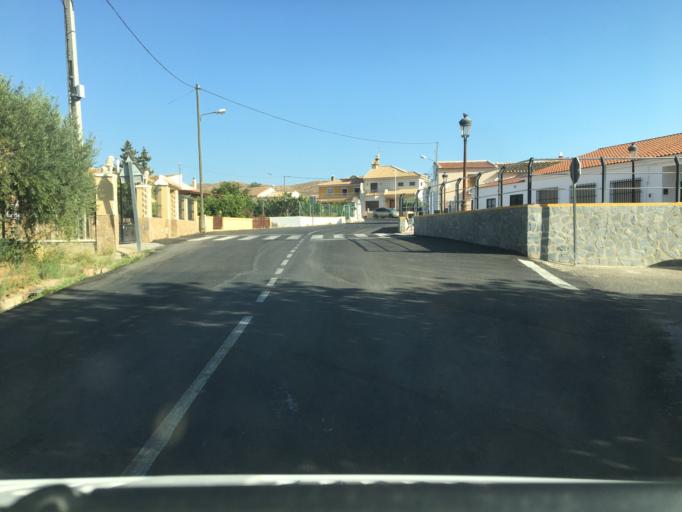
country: ES
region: Andalusia
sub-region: Provincia de Almeria
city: Huercal-Overa
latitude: 37.4697
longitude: -1.8933
